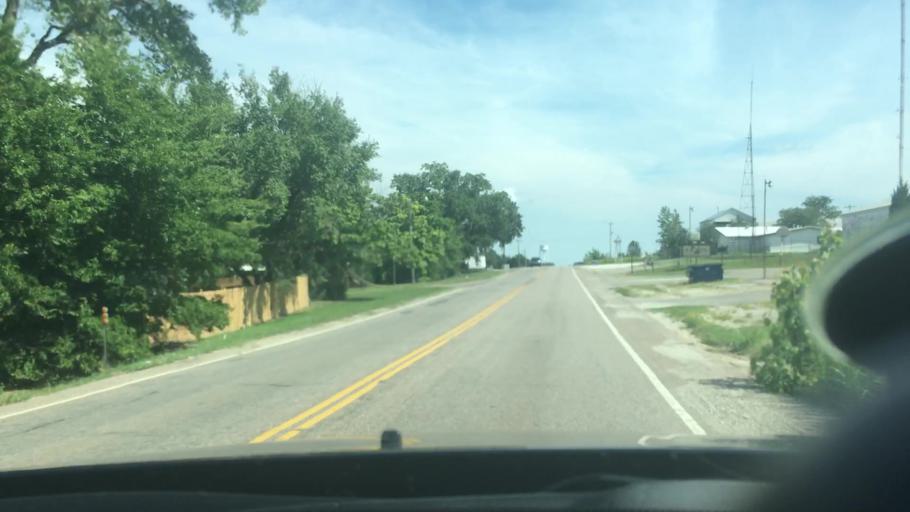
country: US
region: Oklahoma
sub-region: Seminole County
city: Seminole
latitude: 35.2293
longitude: -96.6839
